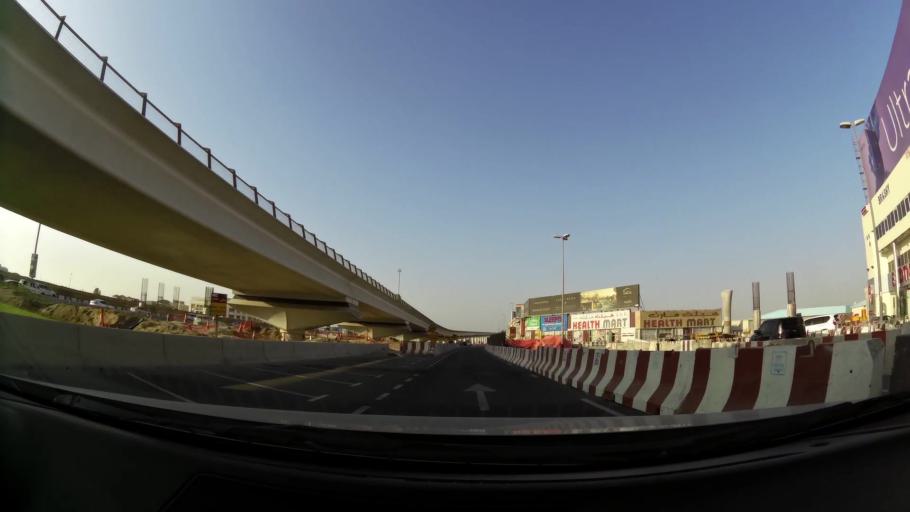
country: AE
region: Dubai
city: Dubai
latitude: 25.1582
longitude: 55.2303
